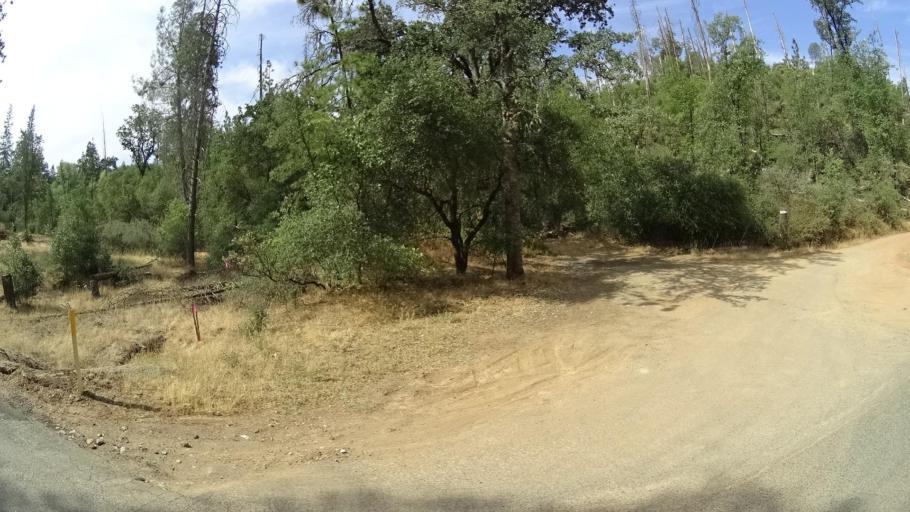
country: US
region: California
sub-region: Mariposa County
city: Mariposa
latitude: 37.5363
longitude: -119.9843
